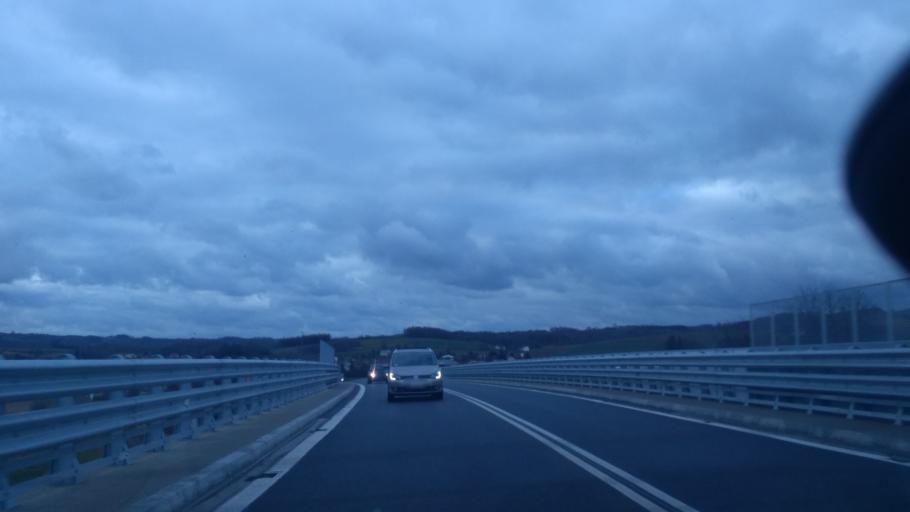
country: PL
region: Subcarpathian Voivodeship
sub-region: Powiat strzyzowski
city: Czudec
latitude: 49.9395
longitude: 21.8200
